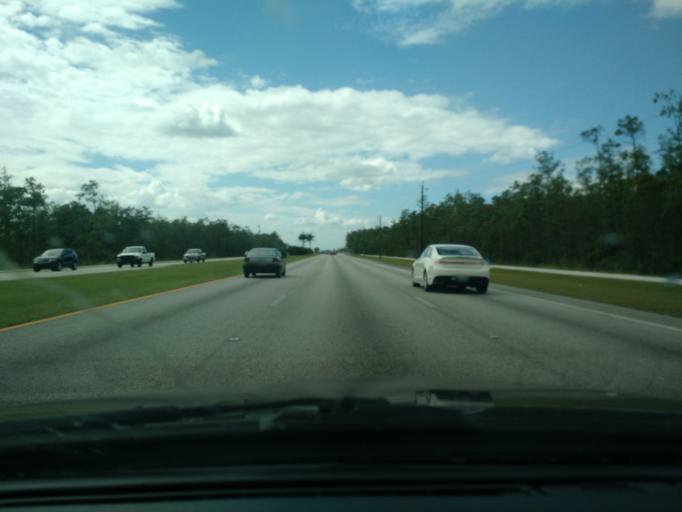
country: US
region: Florida
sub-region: Lee County
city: Gateway
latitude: 26.6131
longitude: -81.7870
